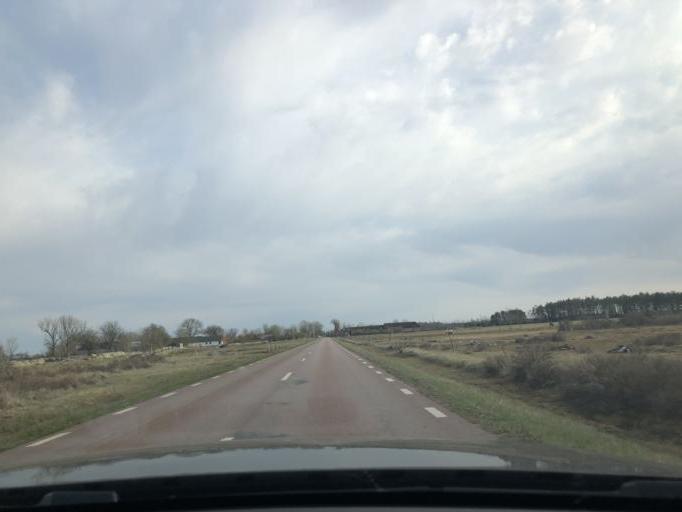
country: SE
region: Kalmar
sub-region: Morbylanga Kommun
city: Sodra Sandby
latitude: 56.5711
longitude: 16.6178
